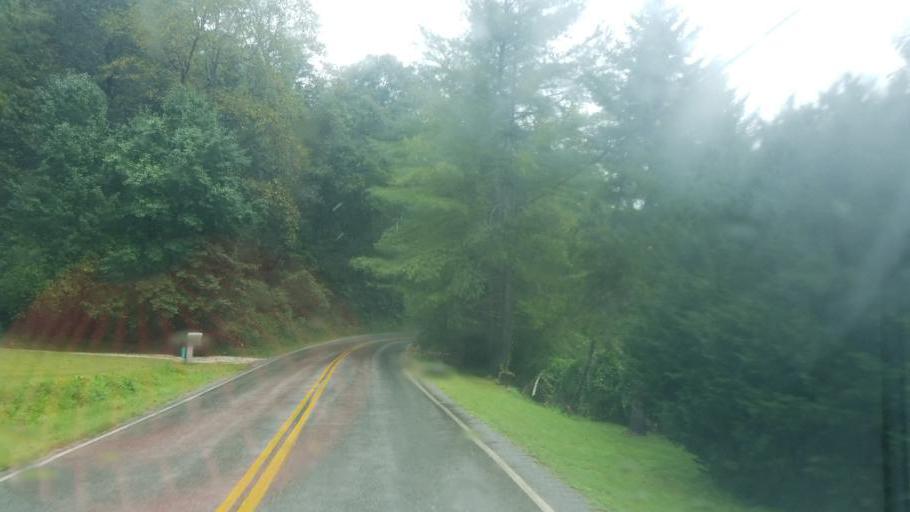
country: US
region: Ohio
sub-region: Scioto County
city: Franklin Furnace
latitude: 38.6617
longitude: -82.9180
